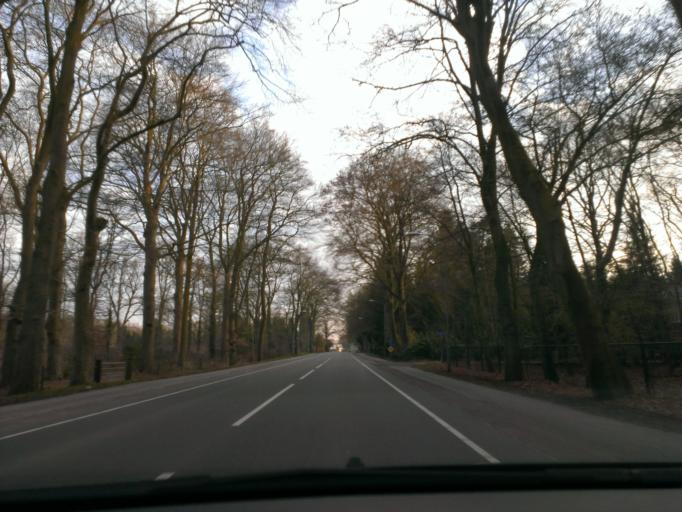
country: NL
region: Gelderland
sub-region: Gemeente Hattem
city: Hattem
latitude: 52.4479
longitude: 6.0699
